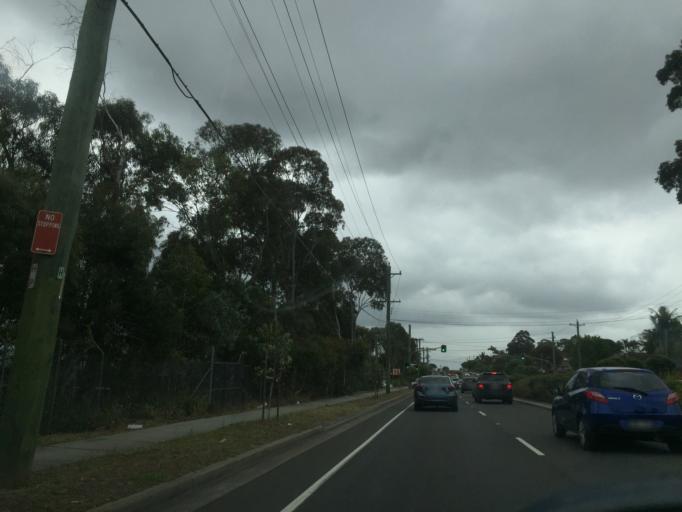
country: AU
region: New South Wales
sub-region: Holroyd
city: Girraween
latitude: -33.7672
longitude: 150.9501
